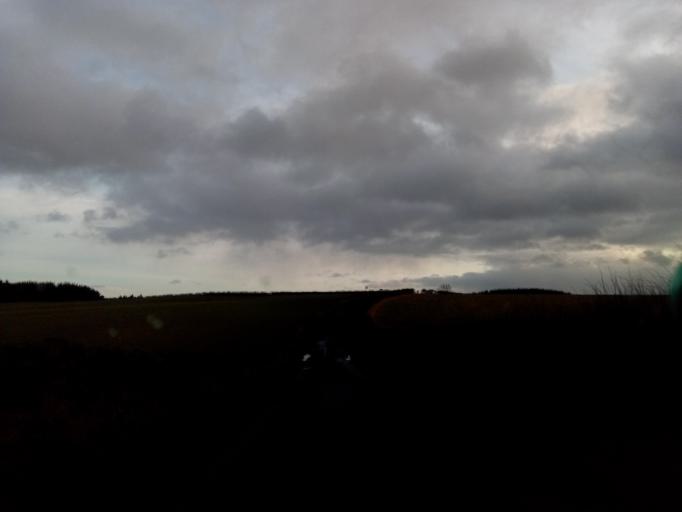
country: GB
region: Scotland
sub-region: The Scottish Borders
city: Selkirk
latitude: 55.5582
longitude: -2.7860
